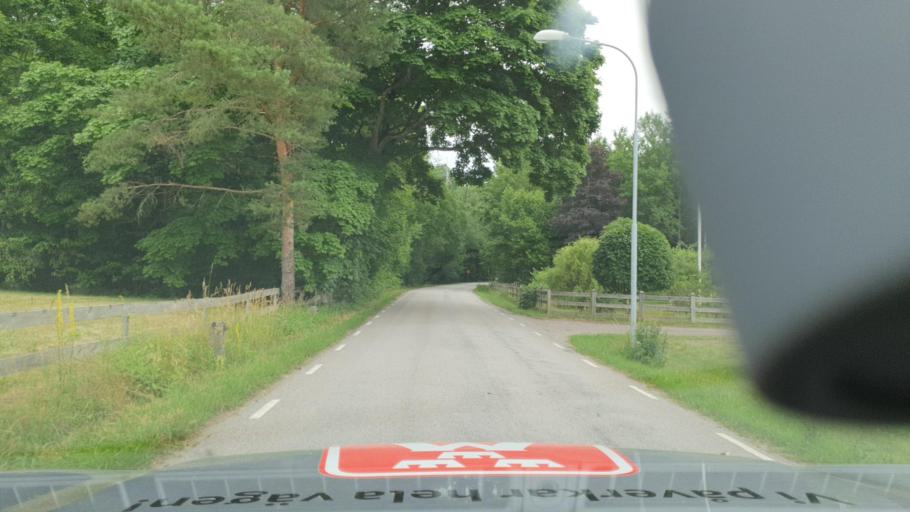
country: SE
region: Kalmar
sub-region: Kalmar Kommun
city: Trekanten
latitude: 56.6166
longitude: 16.0553
